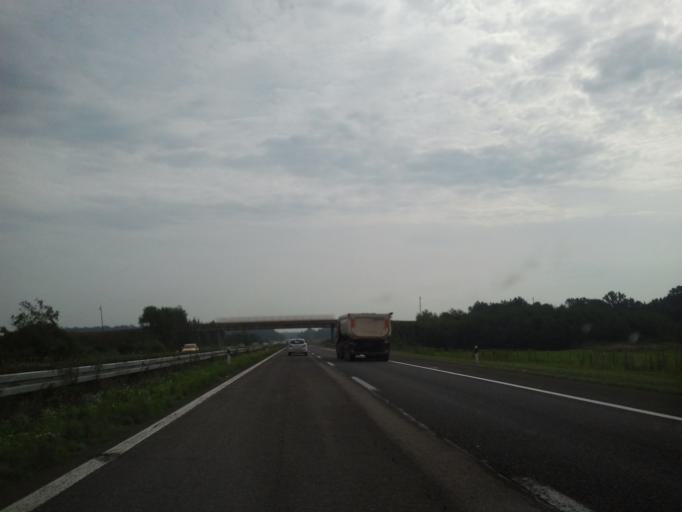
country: HR
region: Grad Zagreb
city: Horvati
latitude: 45.6795
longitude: 15.7724
